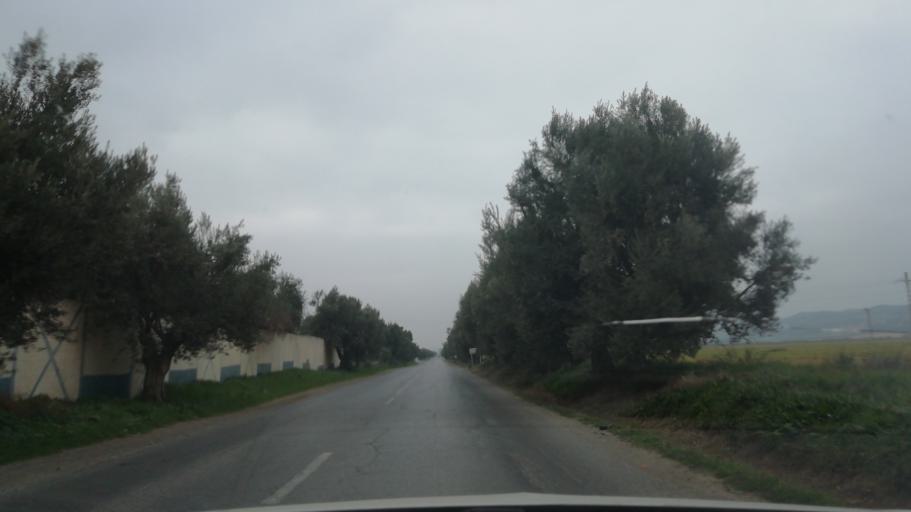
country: DZ
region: Sidi Bel Abbes
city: Sfizef
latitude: 35.2280
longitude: -0.2668
